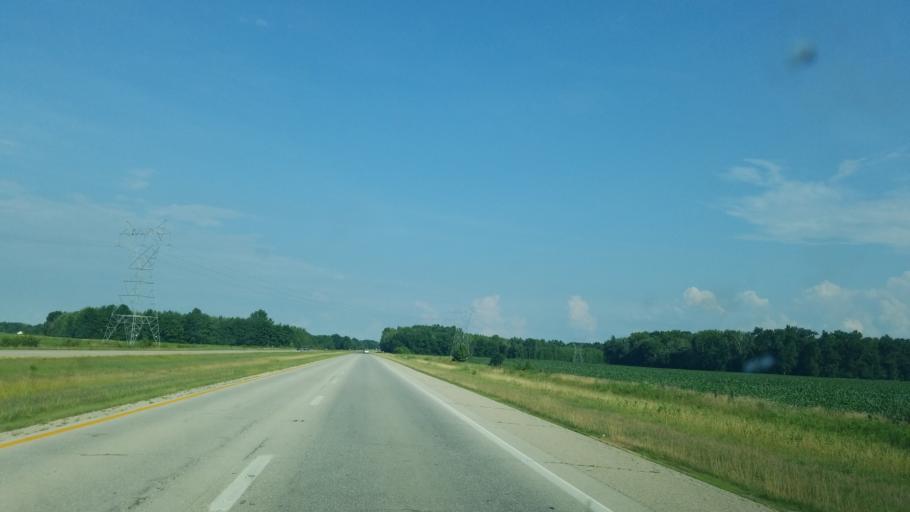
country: US
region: Ohio
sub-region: Brown County
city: Mount Orab
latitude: 39.0324
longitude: -83.8939
